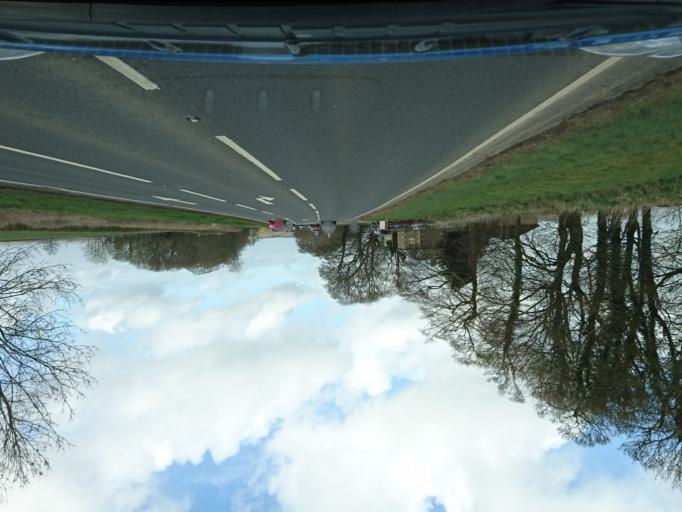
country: GB
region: England
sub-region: South Gloucestershire
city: Cold Ashton
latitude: 51.4698
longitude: -2.3660
